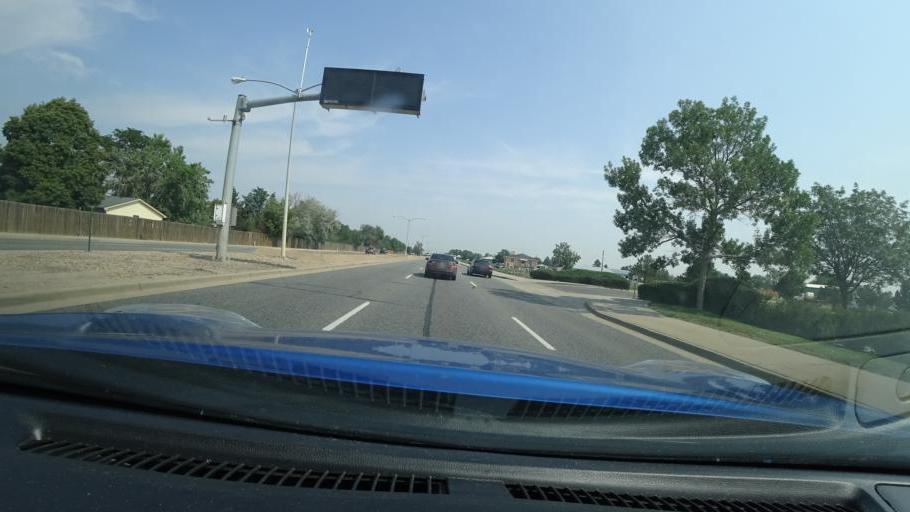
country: US
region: Colorado
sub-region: Adams County
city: Aurora
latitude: 39.7333
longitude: -104.7911
